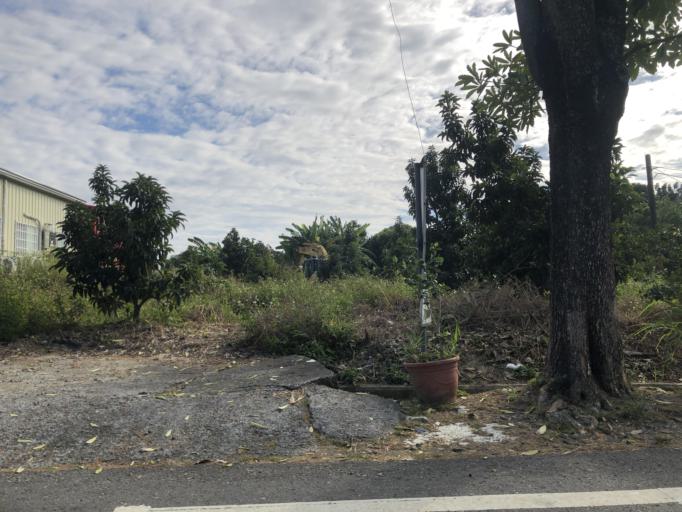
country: TW
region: Taiwan
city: Yujing
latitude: 23.0535
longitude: 120.4148
